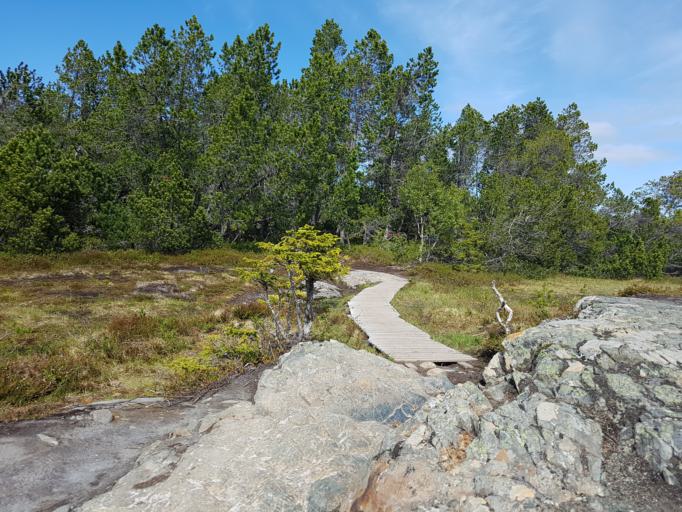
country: NO
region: Sor-Trondelag
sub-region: Trondheim
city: Trondheim
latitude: 63.4310
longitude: 10.3060
